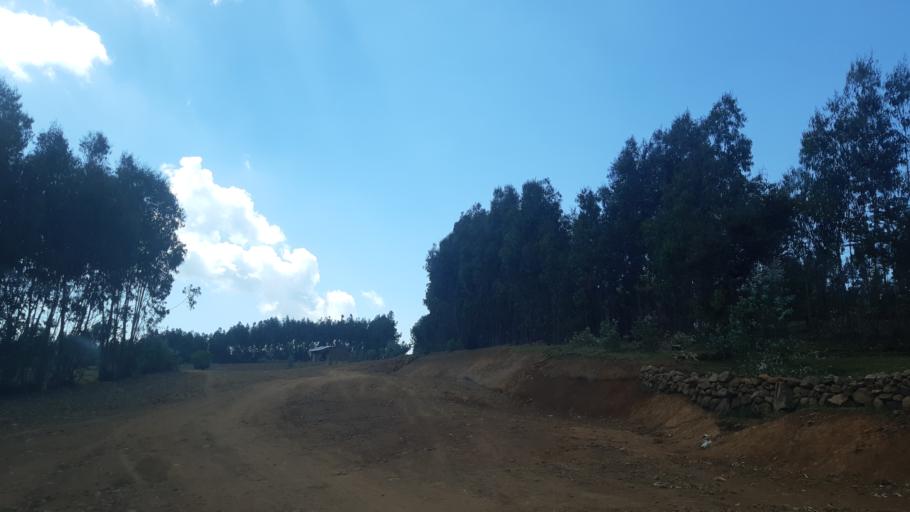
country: ET
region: Amhara
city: Dabat
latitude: 13.3624
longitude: 37.3842
